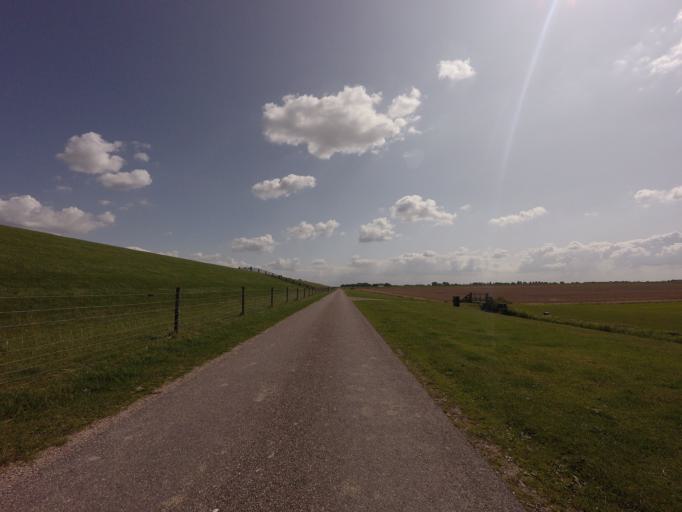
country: NL
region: Friesland
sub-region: Gemeente Ferwerderadiel
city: Hallum
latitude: 53.3211
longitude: 5.7468
